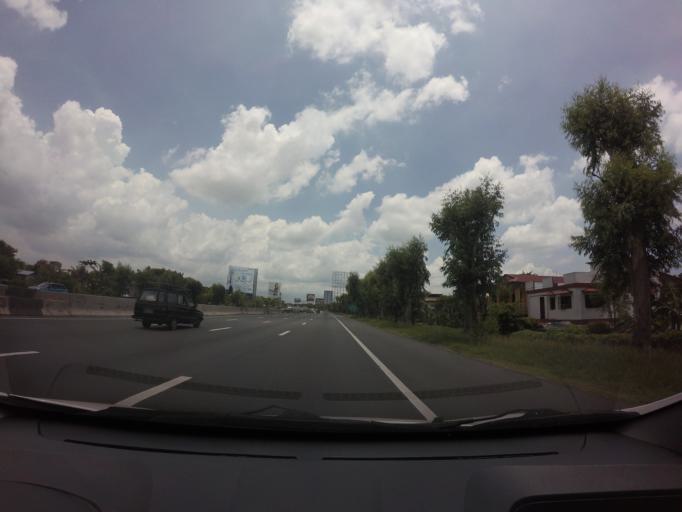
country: PH
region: Calabarzon
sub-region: Province of Laguna
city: San Pedro
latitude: 14.4062
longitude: 121.0406
